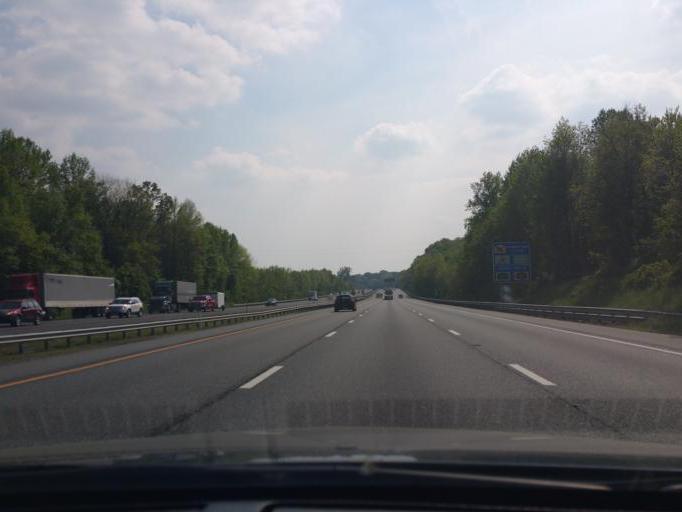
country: US
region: Maryland
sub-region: Harford County
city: Aberdeen
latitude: 39.5521
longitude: -76.1603
